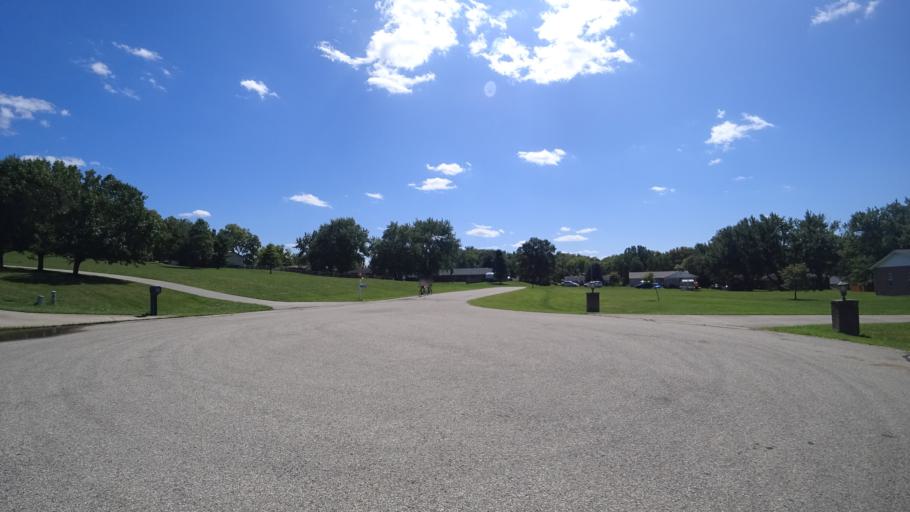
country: US
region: Ohio
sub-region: Butler County
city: New Miami
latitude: 39.4131
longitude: -84.5232
